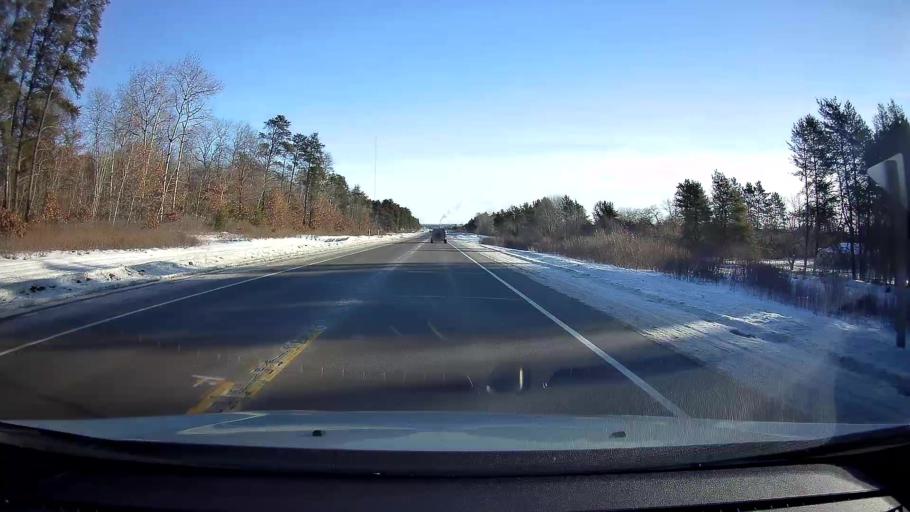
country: US
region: Wisconsin
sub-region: Sawyer County
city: Hayward
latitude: 45.9828
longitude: -91.5497
